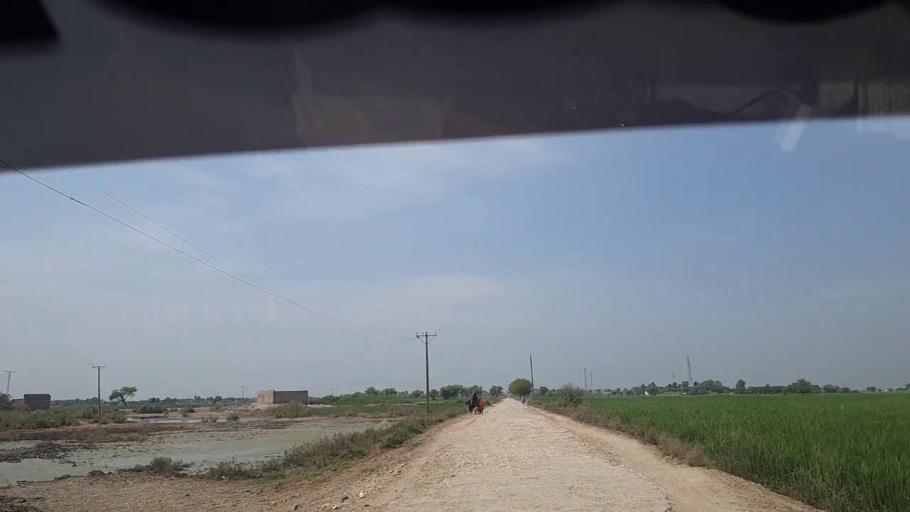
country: PK
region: Sindh
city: Thul
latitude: 28.1751
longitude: 68.7399
